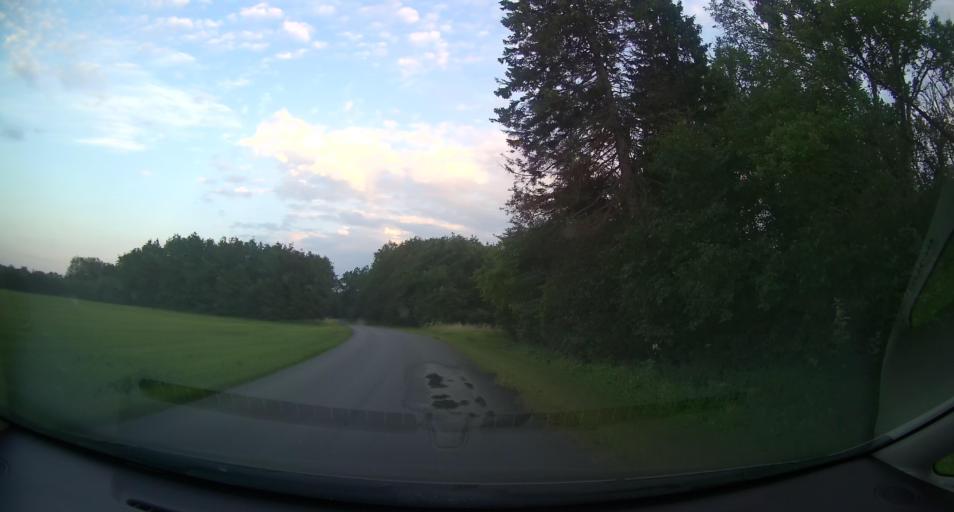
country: EE
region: Laeaene
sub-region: Lihula vald
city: Lihula
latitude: 58.5926
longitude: 23.6101
